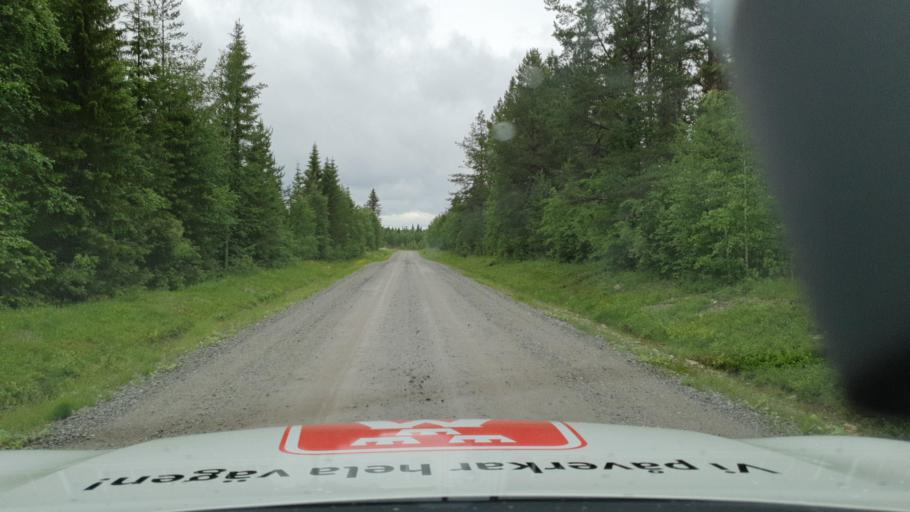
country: SE
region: Vaesterbotten
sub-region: Dorotea Kommun
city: Dorotea
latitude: 64.0858
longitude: 16.6793
